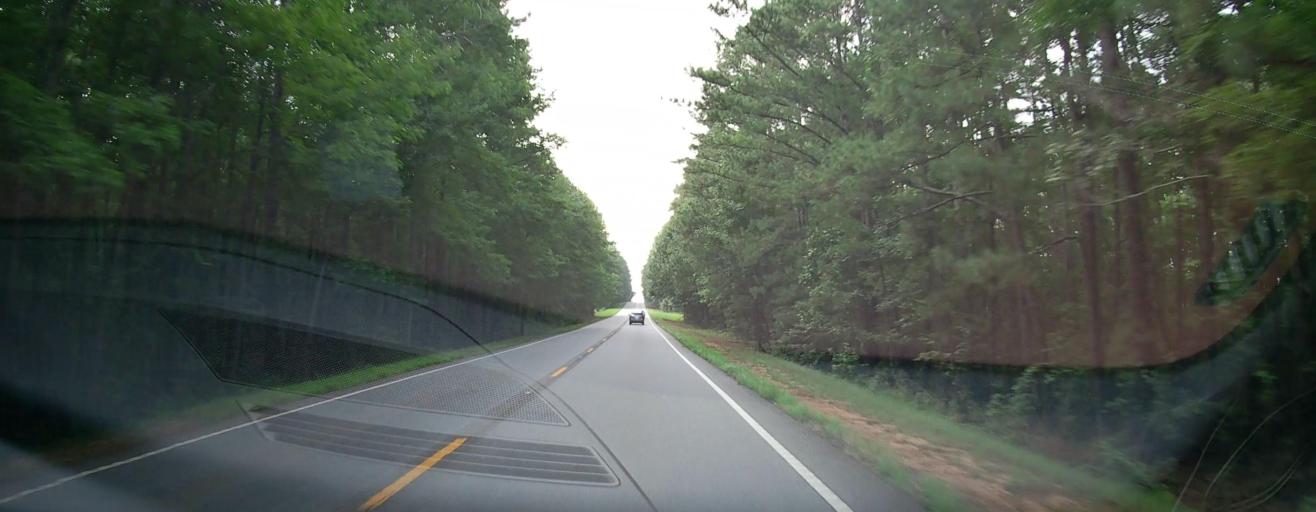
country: US
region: Georgia
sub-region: Monroe County
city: Forsyth
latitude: 33.0498
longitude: -83.7619
